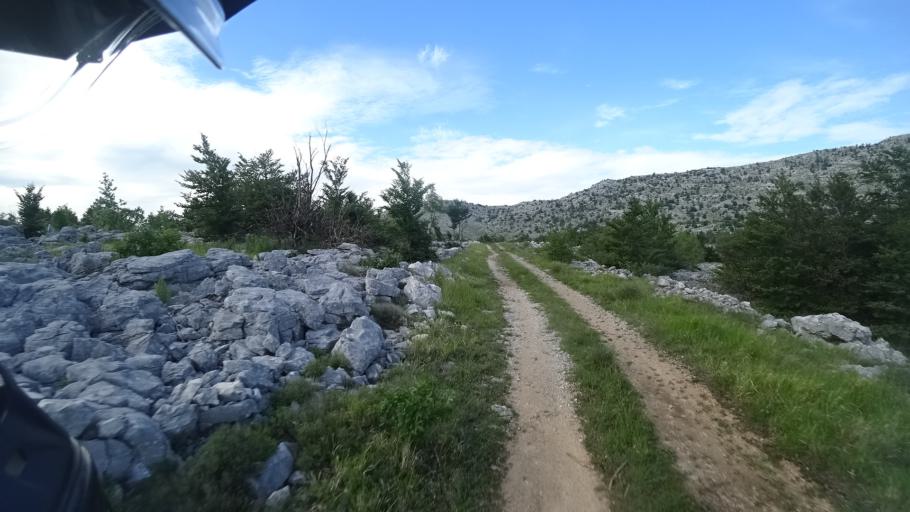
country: HR
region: Splitsko-Dalmatinska
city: Hrvace
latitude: 43.8059
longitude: 16.4336
